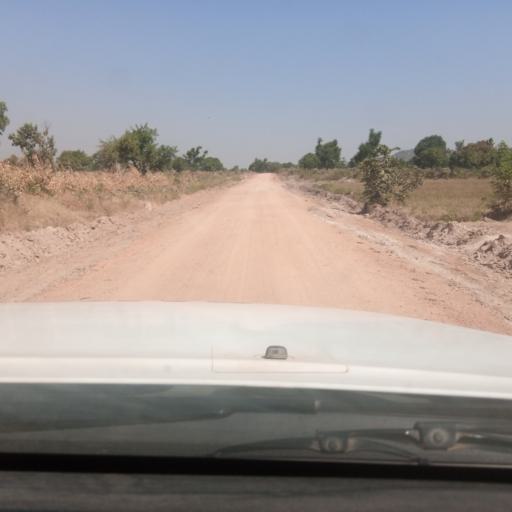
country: NG
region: Adamawa
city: Yola
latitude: 9.0517
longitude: 12.3874
